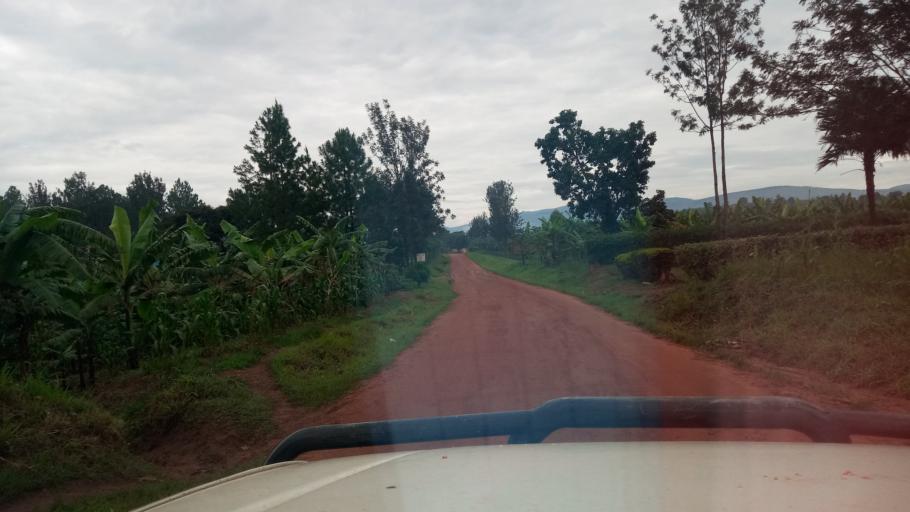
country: UG
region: Western Region
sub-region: Buhweju District
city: Buhweju
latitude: -0.1698
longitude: 30.4629
